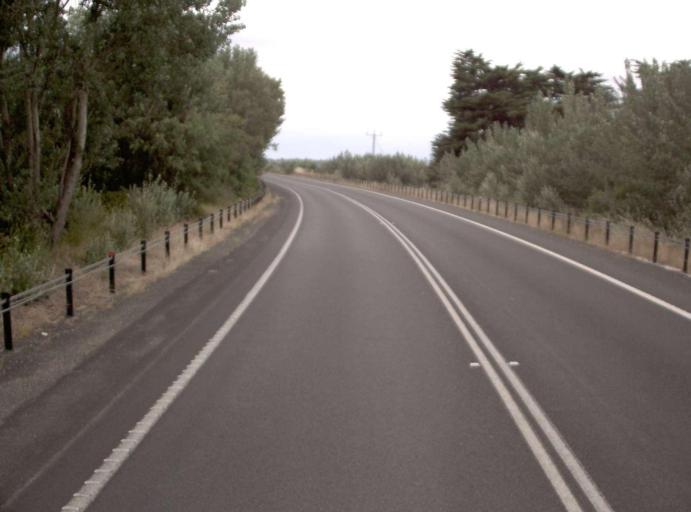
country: AU
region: Victoria
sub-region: East Gippsland
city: Bairnsdale
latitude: -37.8383
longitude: 147.6396
